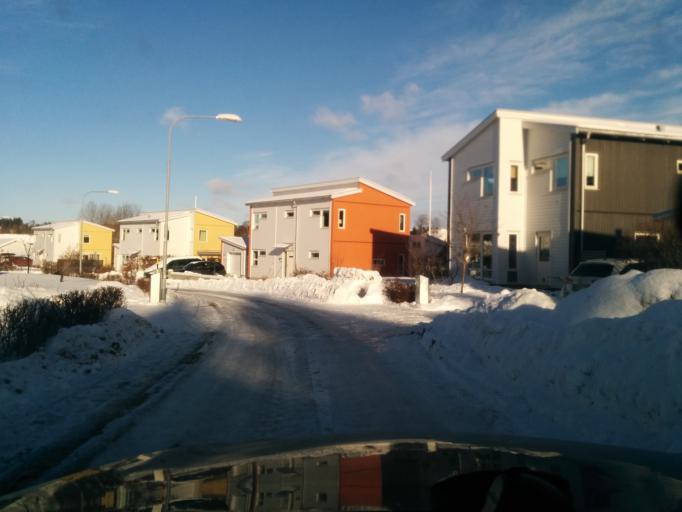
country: SE
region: Stockholm
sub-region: Vallentuna Kommun
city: Vallentuna
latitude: 59.4956
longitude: 18.0819
